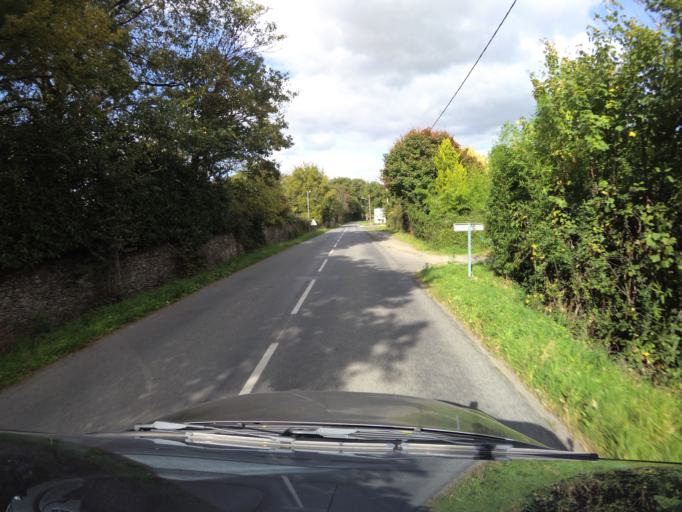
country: FR
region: Pays de la Loire
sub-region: Departement de la Loire-Atlantique
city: Casson
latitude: 47.3818
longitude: -1.5602
